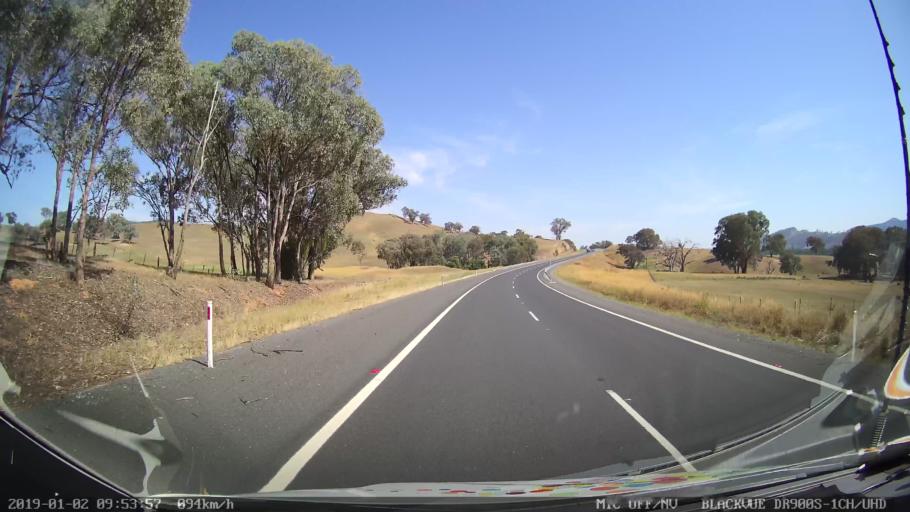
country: AU
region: New South Wales
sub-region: Tumut Shire
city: Tumut
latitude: -35.2417
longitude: 148.1988
